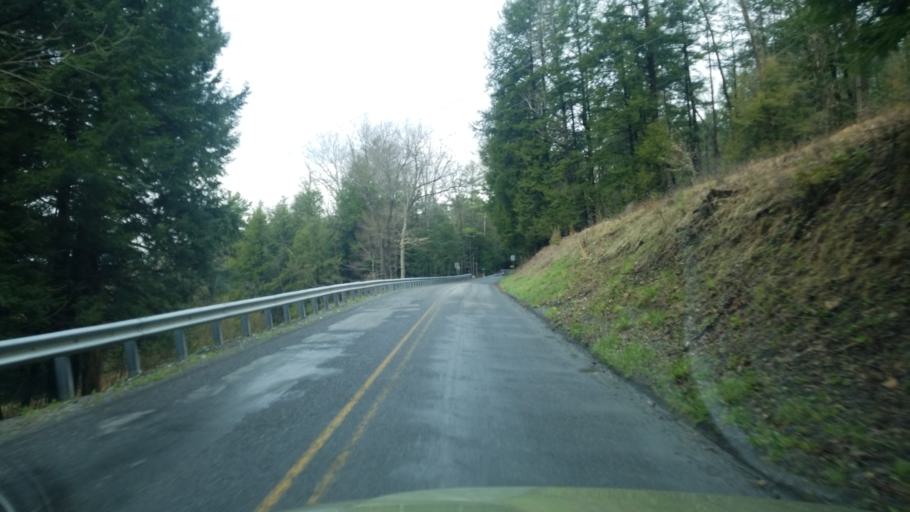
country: US
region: Pennsylvania
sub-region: Clearfield County
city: Clearfield
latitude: 41.0664
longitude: -78.4207
